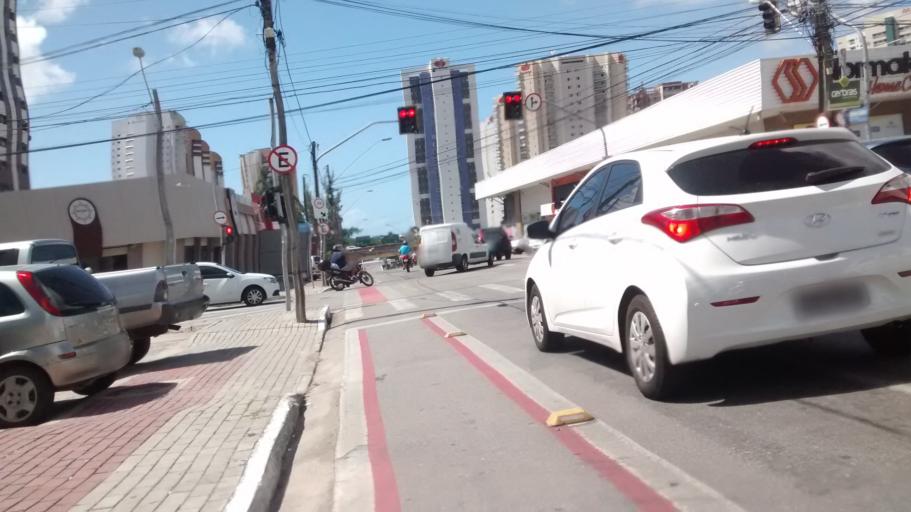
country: BR
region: Ceara
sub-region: Fortaleza
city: Fortaleza
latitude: -3.7478
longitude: -38.4948
